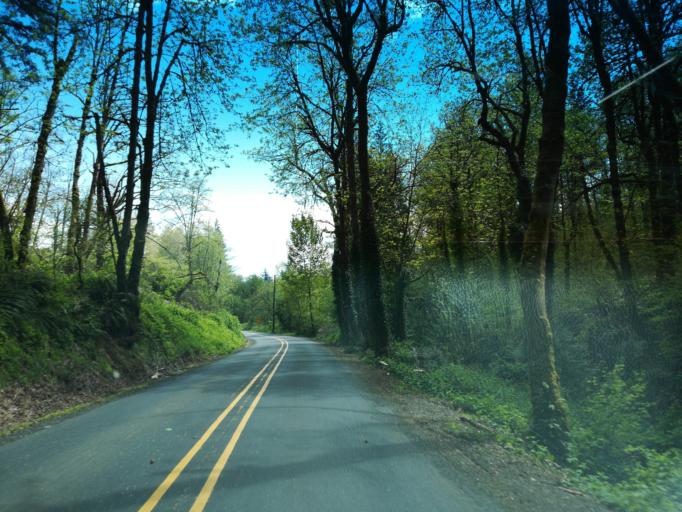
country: US
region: Oregon
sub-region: Clackamas County
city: Damascus
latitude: 45.4485
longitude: -122.4402
